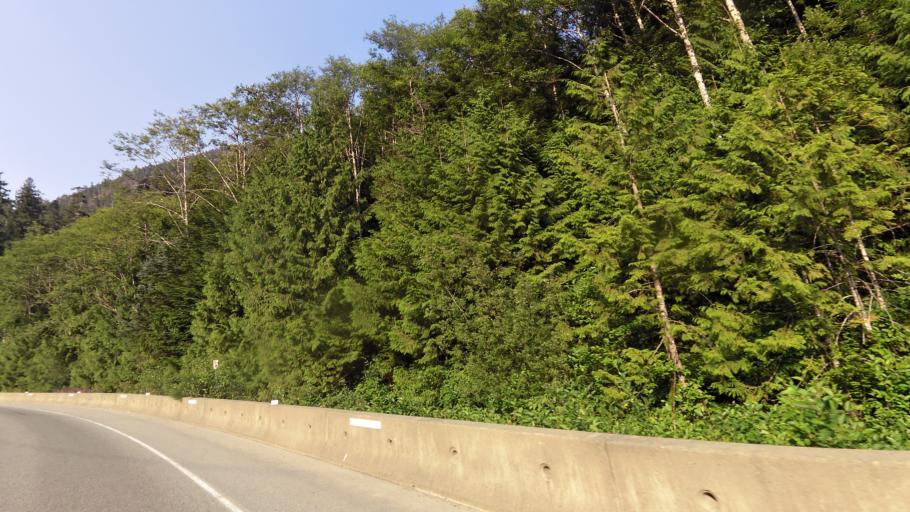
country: CA
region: British Columbia
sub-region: Regional District of Alberni-Clayoquot
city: Ucluelet
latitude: 49.2144
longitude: -125.3674
